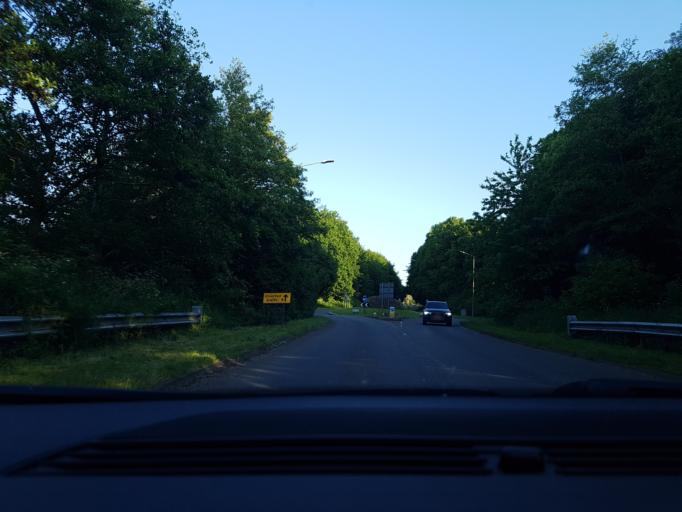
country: GB
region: England
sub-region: Buckinghamshire
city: Buckingham
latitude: 51.9948
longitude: -0.9693
